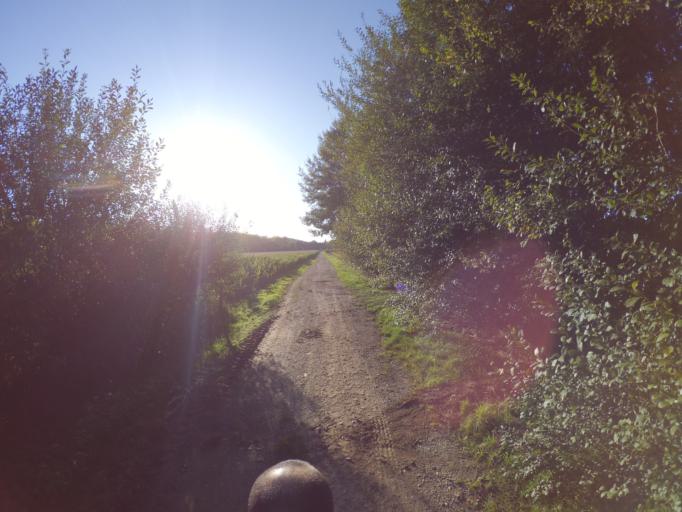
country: FR
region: Brittany
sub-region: Departement du Morbihan
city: Saint-Vincent-sur-Oust
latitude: 47.7238
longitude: -2.1747
